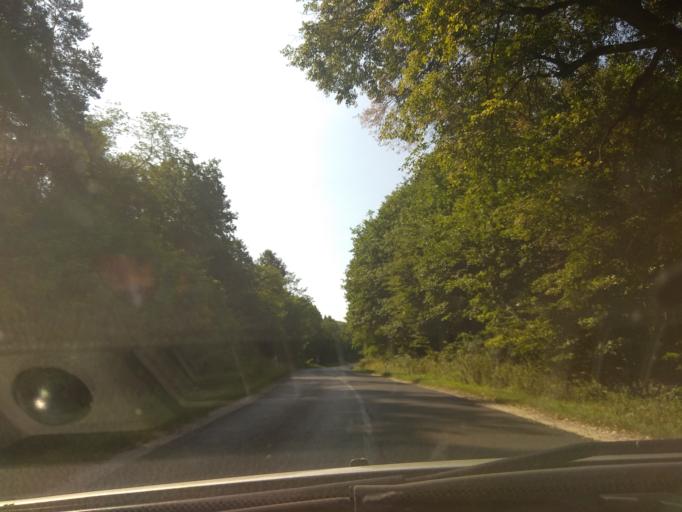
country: HU
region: Borsod-Abauj-Zemplen
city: Harsany
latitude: 47.9939
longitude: 20.7537
